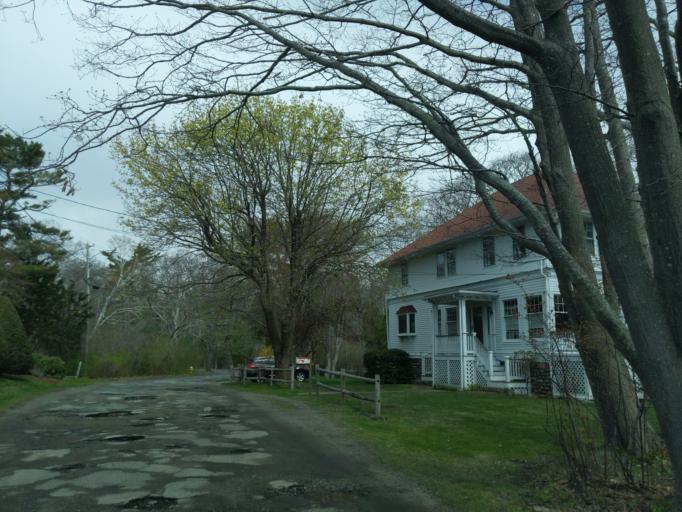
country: US
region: Massachusetts
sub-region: Essex County
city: Rockport
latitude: 42.6391
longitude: -70.6027
